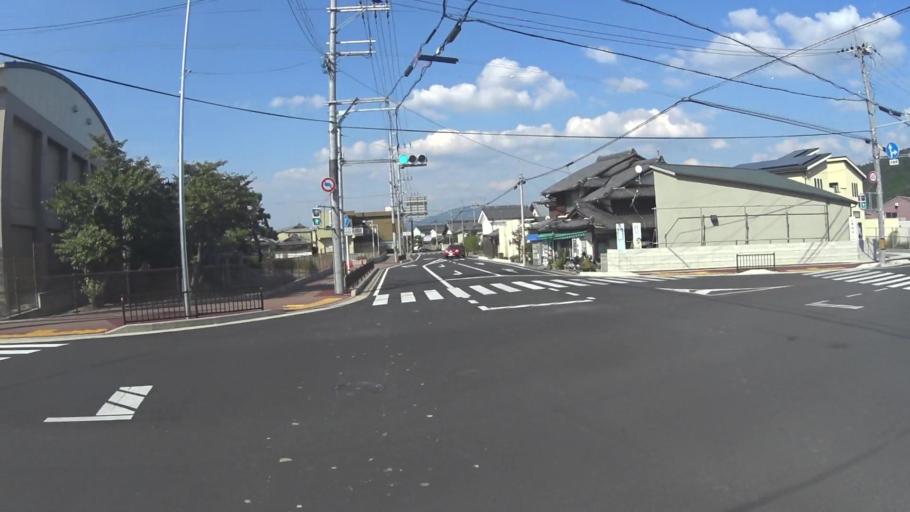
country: JP
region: Kyoto
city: Kameoka
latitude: 34.9973
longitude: 135.5491
